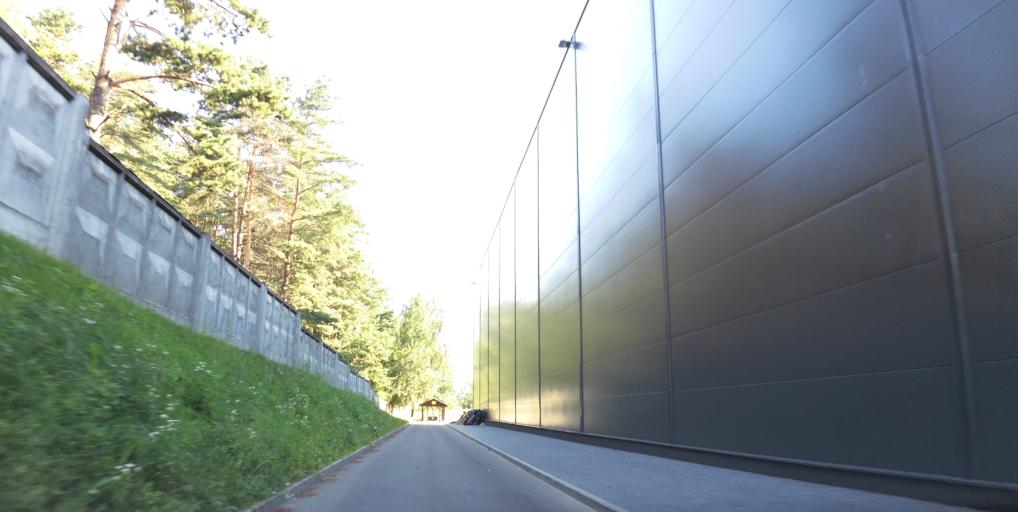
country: LT
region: Vilnius County
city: Seskine
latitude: 54.7084
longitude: 25.2336
